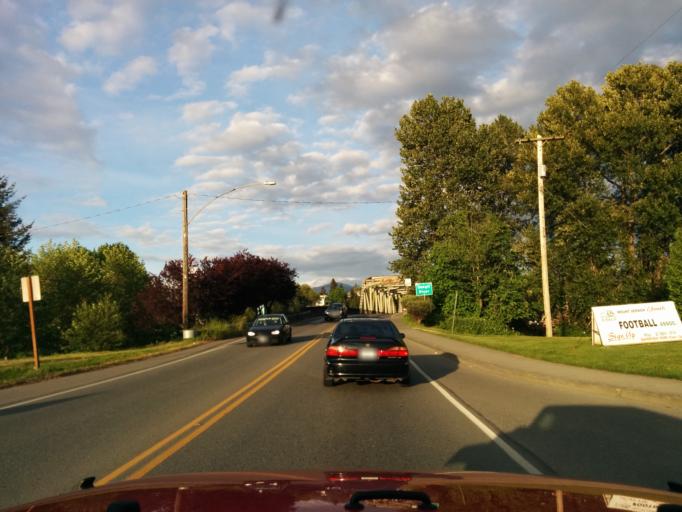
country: US
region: Washington
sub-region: Skagit County
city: Mount Vernon
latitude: 48.4217
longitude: -122.3420
